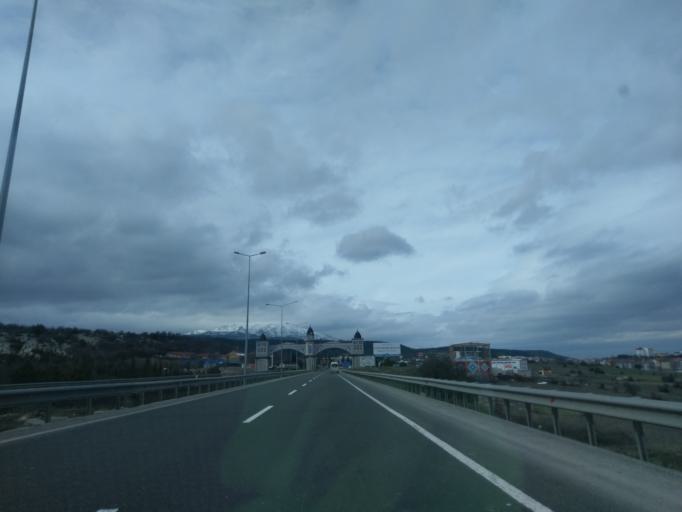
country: TR
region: Kuetahya
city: Kutahya
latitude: 39.3760
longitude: 30.0589
